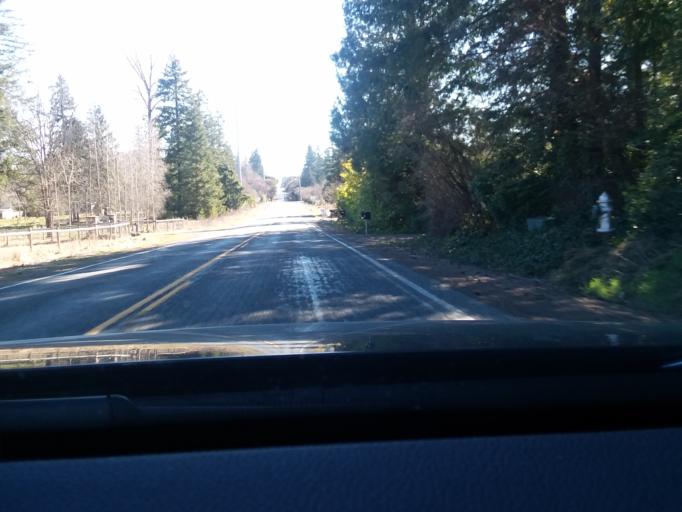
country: US
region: Washington
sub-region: Pierce County
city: Waller
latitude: 47.1807
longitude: -122.3820
